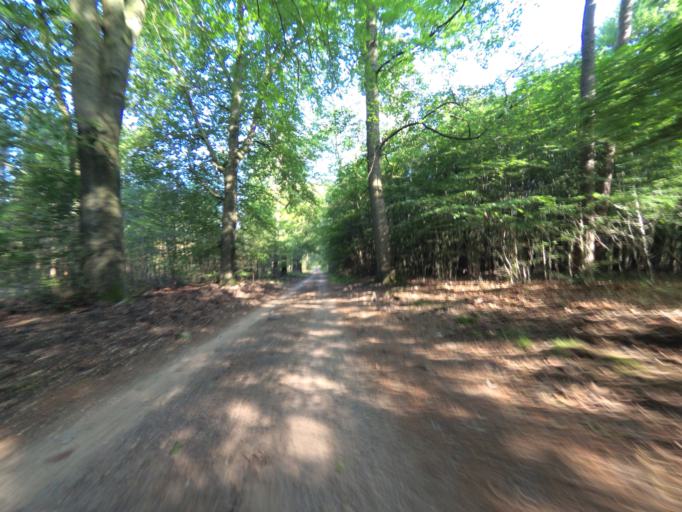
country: NL
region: Gelderland
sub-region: Gemeente Apeldoorn
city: Beekbergen
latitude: 52.1666
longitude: 5.8720
